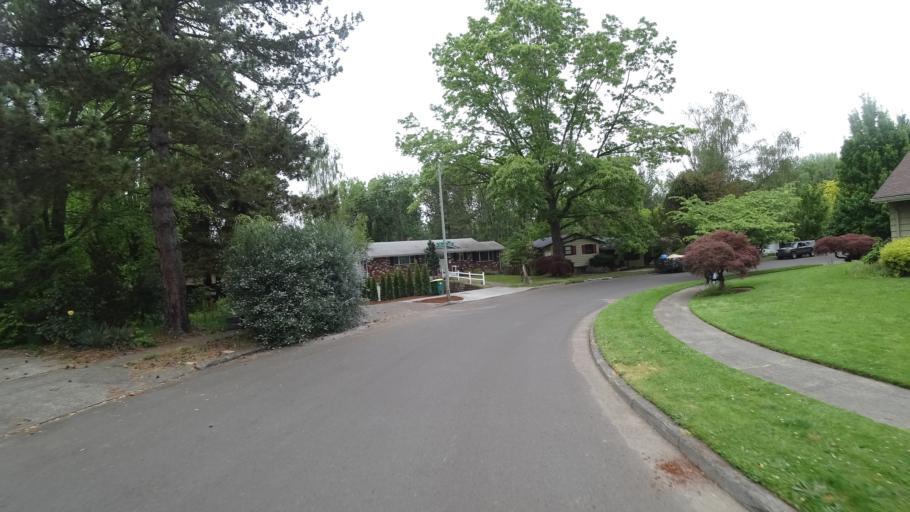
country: US
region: Oregon
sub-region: Washington County
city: Raleigh Hills
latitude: 45.4832
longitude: -122.7796
